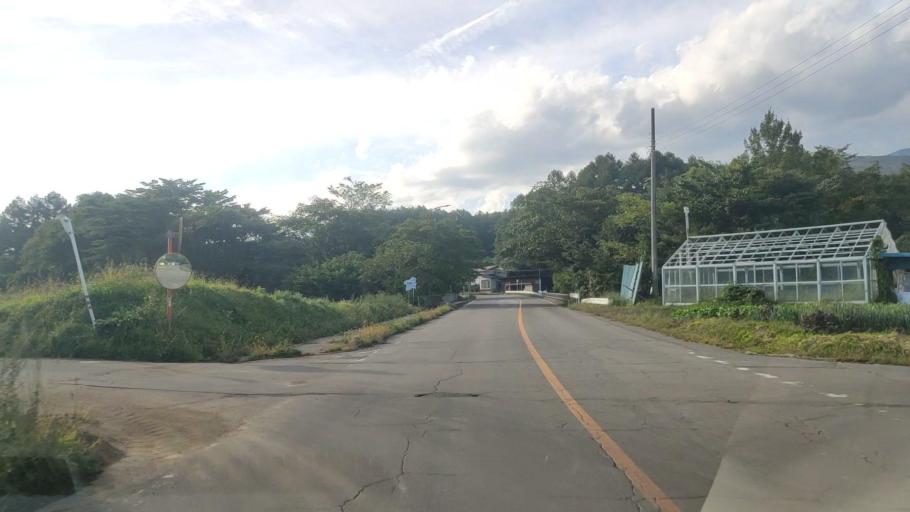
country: JP
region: Nagano
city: Komoro
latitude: 36.4867
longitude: 138.4460
